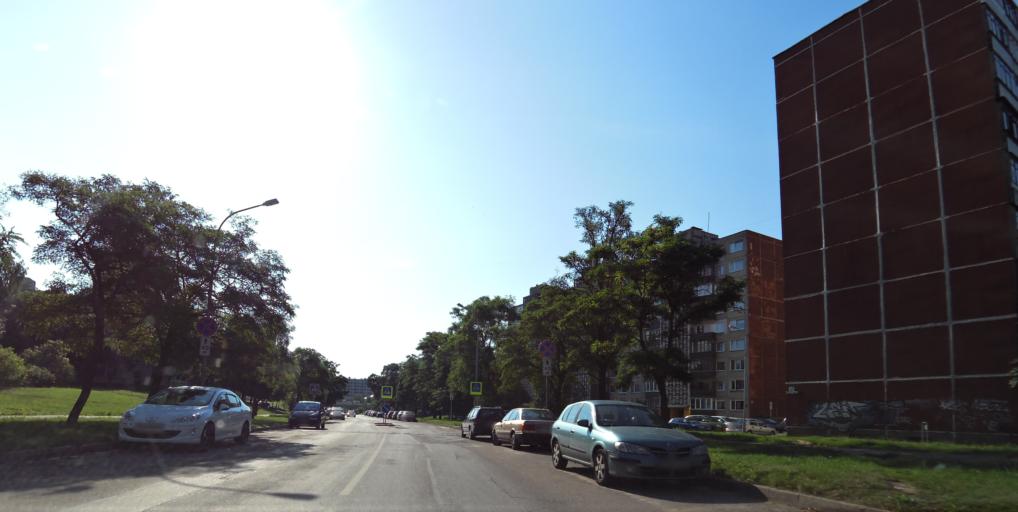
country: LT
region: Vilnius County
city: Justiniskes
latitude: 54.6959
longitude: 25.2139
